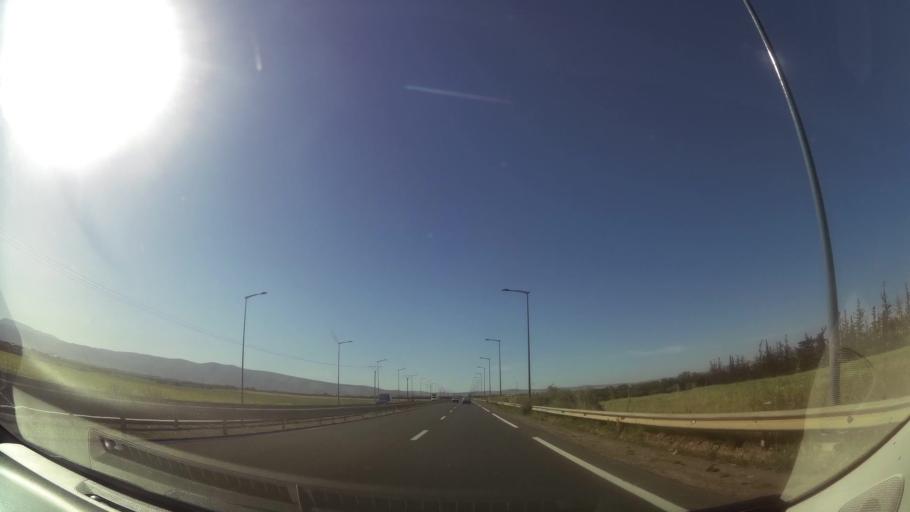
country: MA
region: Oriental
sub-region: Oujda-Angad
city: Oujda
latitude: 34.8317
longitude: -1.9751
